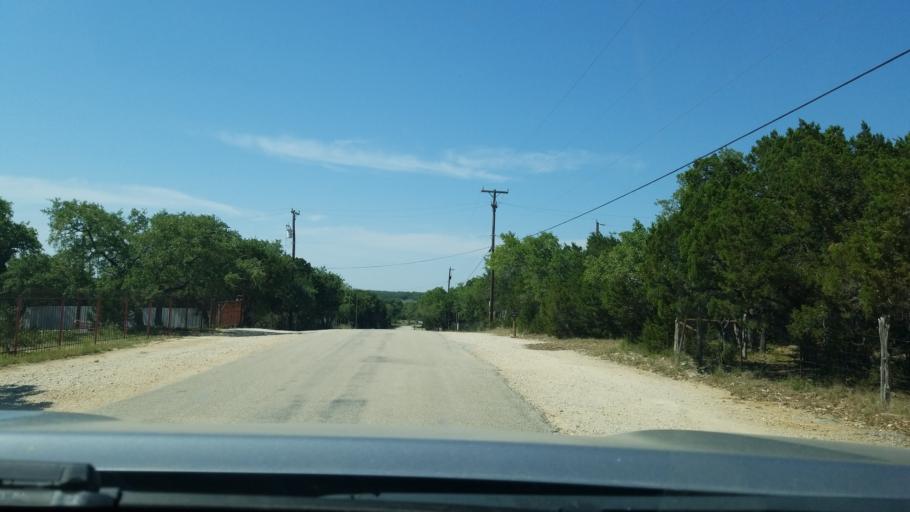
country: US
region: Texas
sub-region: Comal County
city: Bulverde
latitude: 29.7660
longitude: -98.5153
